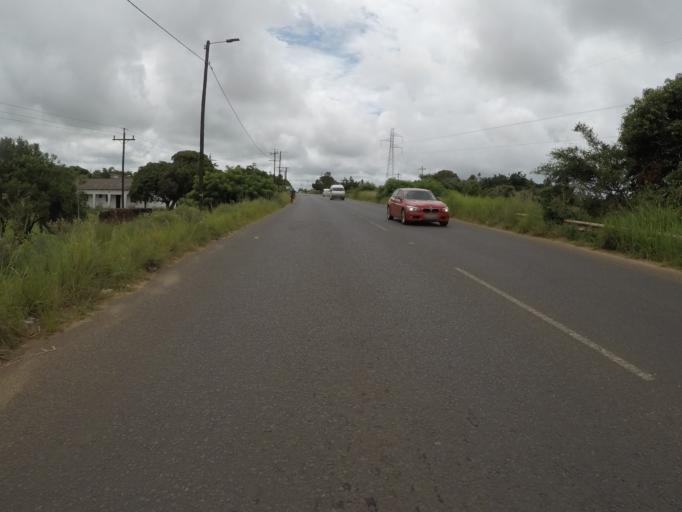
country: ZA
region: KwaZulu-Natal
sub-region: uThungulu District Municipality
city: eSikhawini
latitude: -28.8443
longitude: 31.9328
